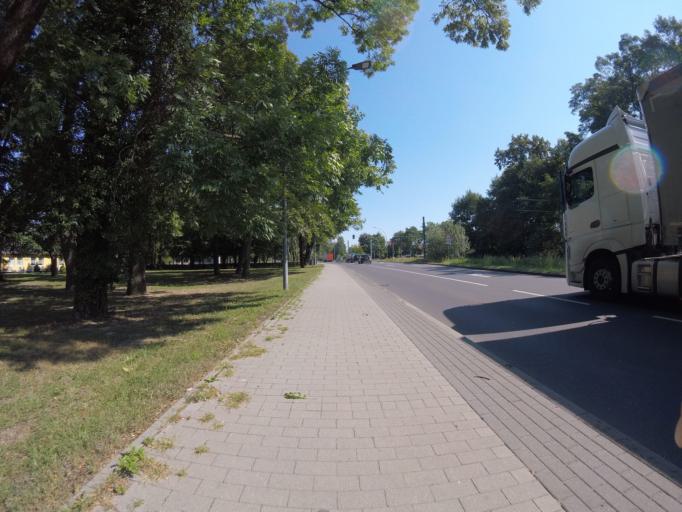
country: DE
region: Brandenburg
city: Mullrose
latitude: 52.2945
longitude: 14.4697
